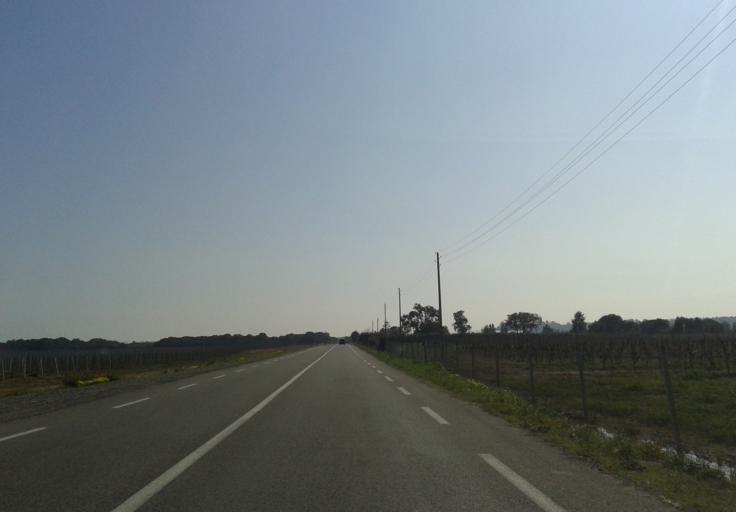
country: FR
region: Corsica
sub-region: Departement de la Haute-Corse
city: Cervione
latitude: 42.2827
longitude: 9.5506
